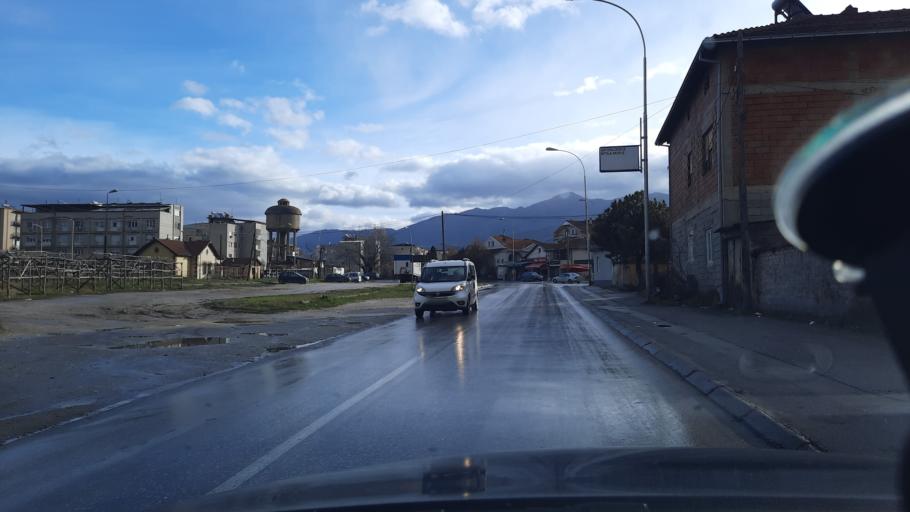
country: MK
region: Prilep
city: Markov Grad
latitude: 41.3433
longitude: 21.5395
